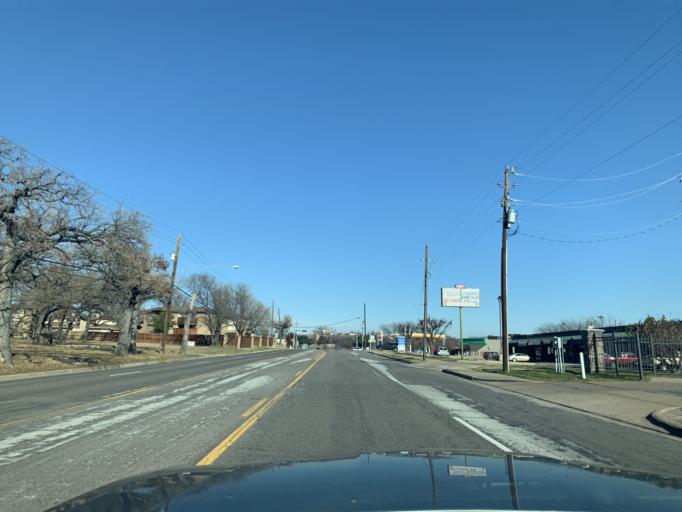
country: US
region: Texas
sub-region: Tarrant County
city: Bedford
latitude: 32.8432
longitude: -97.1447
